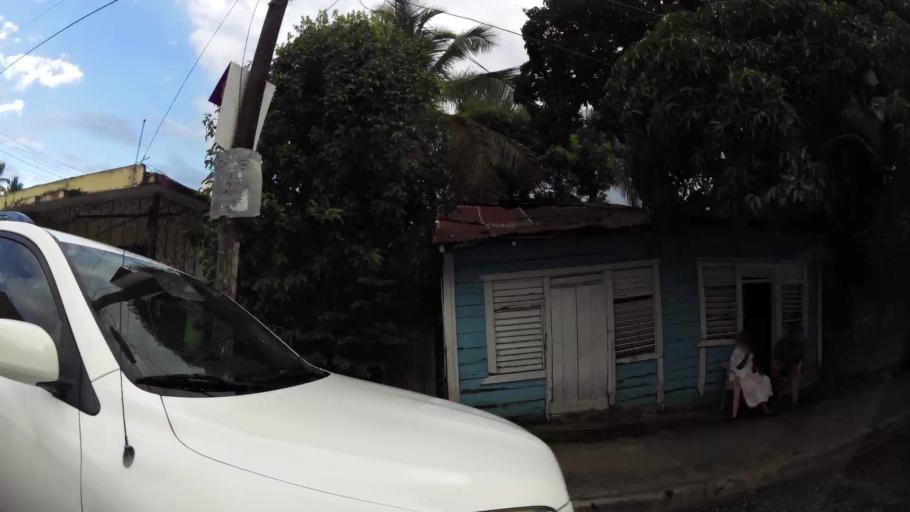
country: DO
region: San Cristobal
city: Villa Altagracia
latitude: 18.6697
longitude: -70.1743
